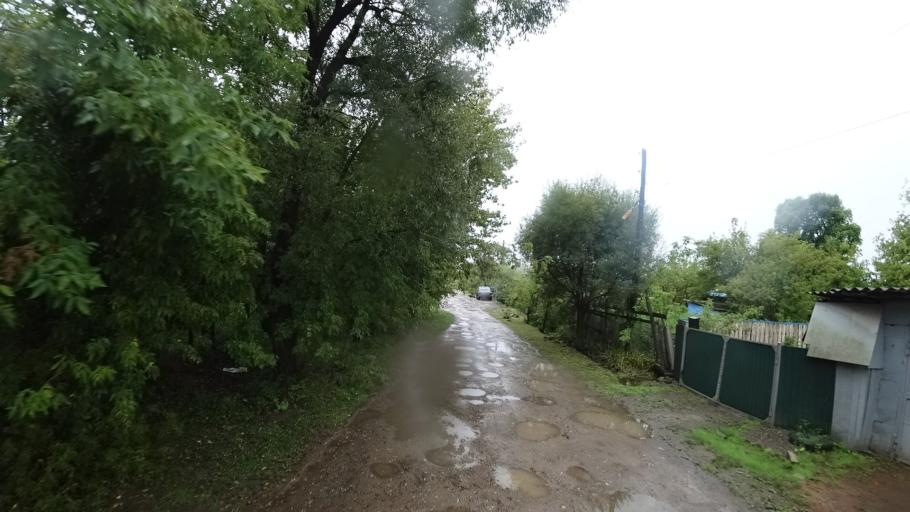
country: RU
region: Primorskiy
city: Monastyrishche
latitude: 44.2578
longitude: 132.4280
